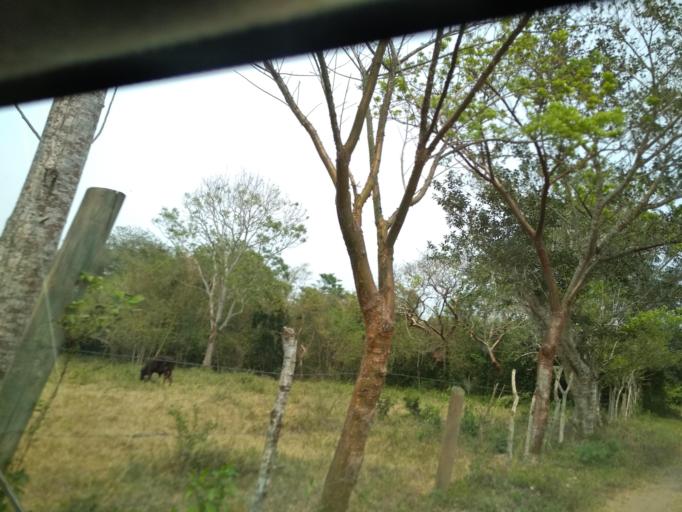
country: MX
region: Veracruz
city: El Tejar
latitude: 19.0591
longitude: -96.1512
